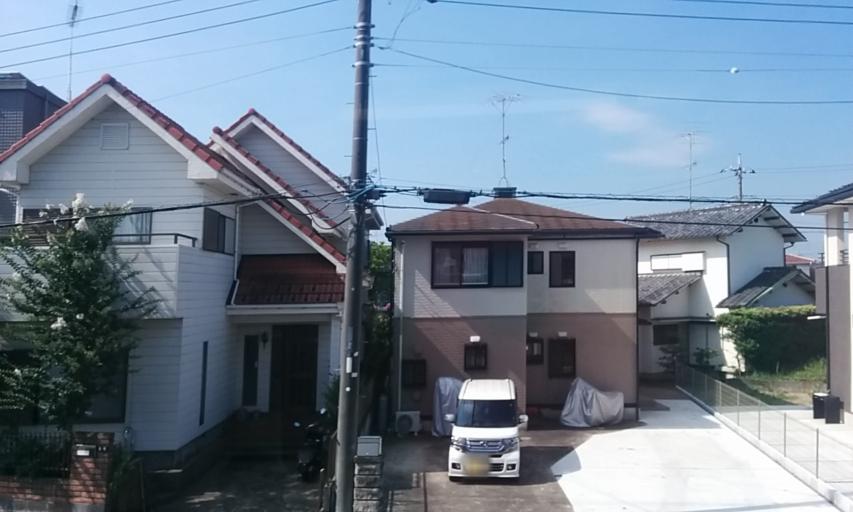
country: JP
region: Saitama
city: Kazo
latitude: 36.1088
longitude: 139.6368
